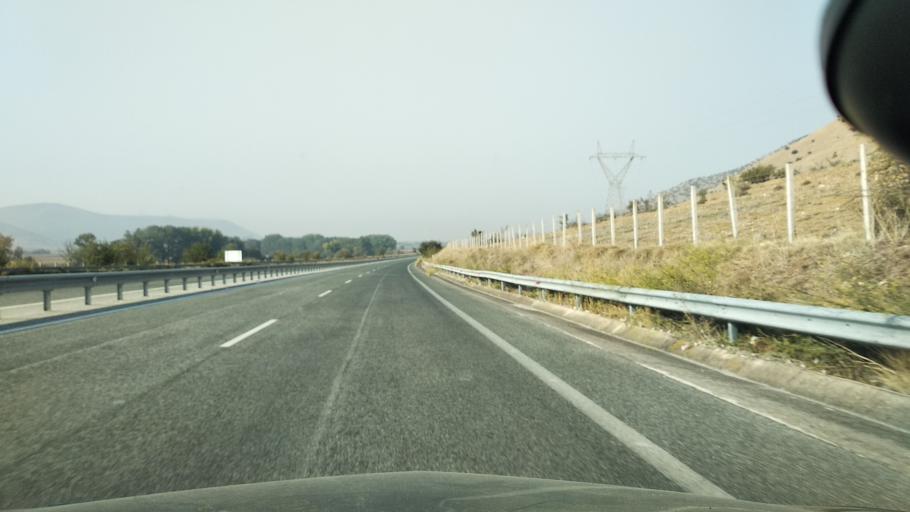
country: GR
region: Thessaly
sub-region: Trikala
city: Zarkos
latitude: 39.5898
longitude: 22.1646
